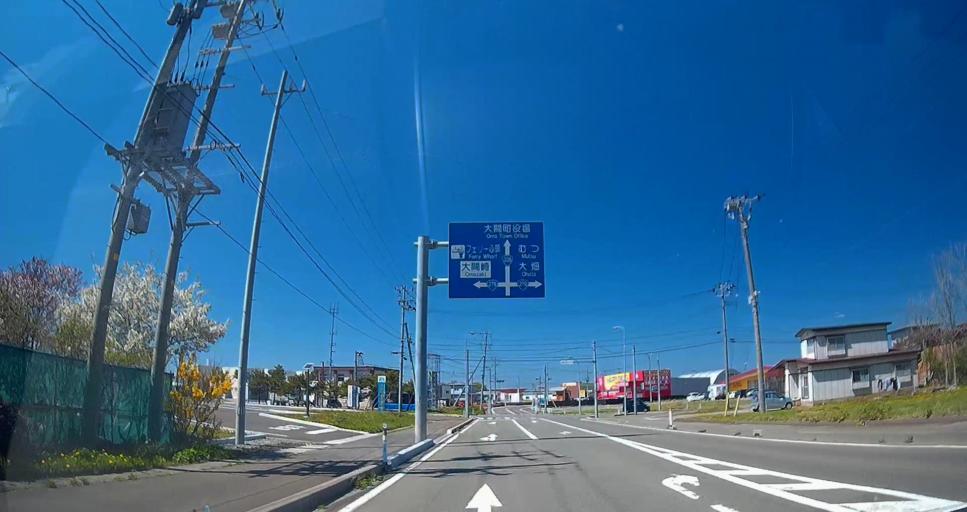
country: JP
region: Hokkaido
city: Hakodate
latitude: 41.5222
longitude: 140.9057
